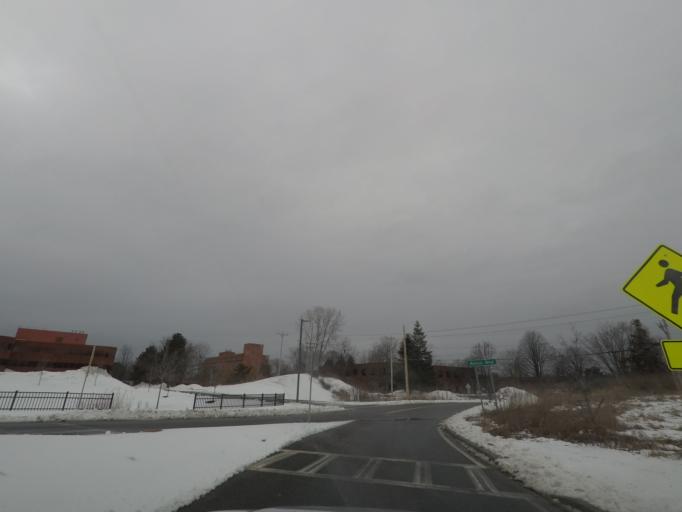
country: US
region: New York
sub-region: Albany County
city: Roessleville
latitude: 42.7213
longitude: -73.7967
